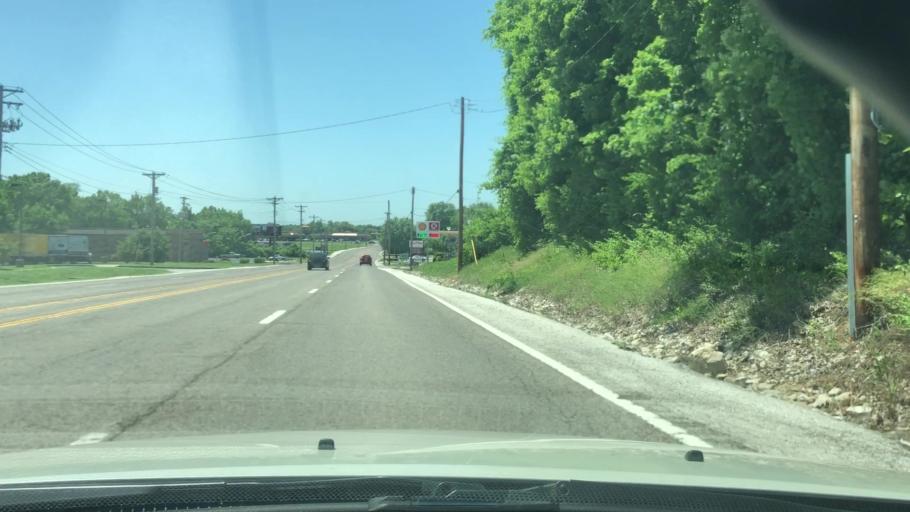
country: US
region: Missouri
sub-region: Jefferson County
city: Arnold
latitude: 38.4695
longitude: -90.3556
